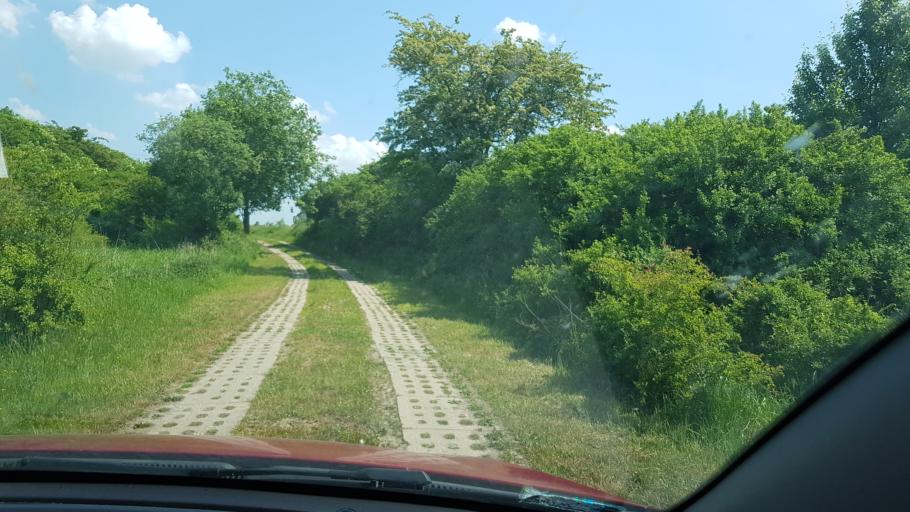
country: PL
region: West Pomeranian Voivodeship
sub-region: Powiat gryficki
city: Trzebiatow
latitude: 54.0970
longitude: 15.2206
